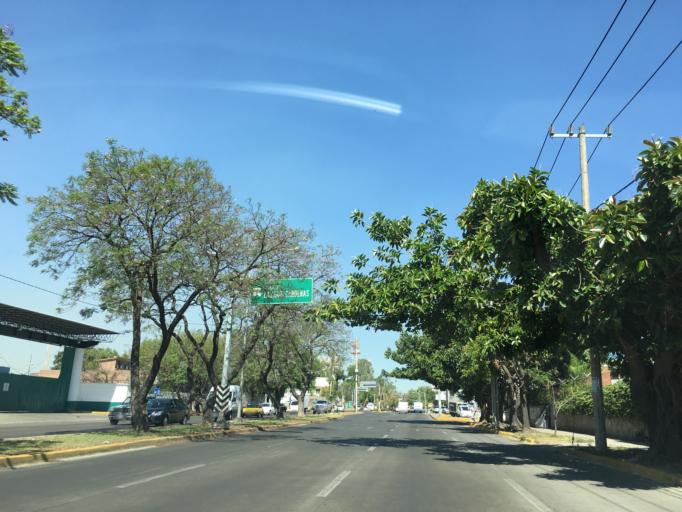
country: MX
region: Jalisco
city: Guadalajara
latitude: 20.6650
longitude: -103.3708
